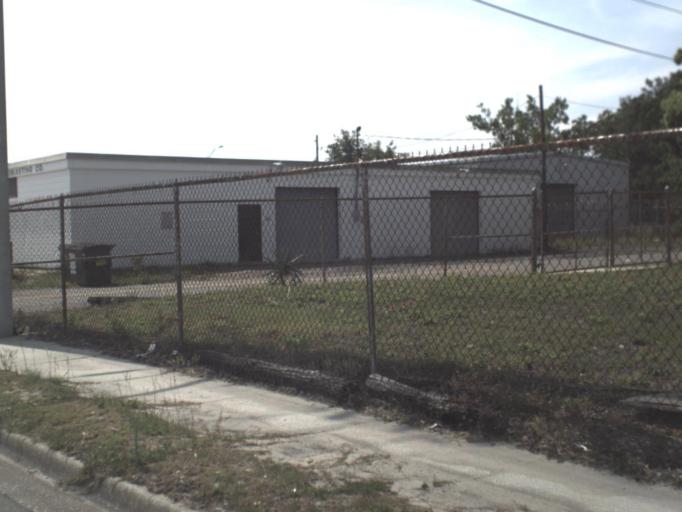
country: US
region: Florida
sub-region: Duval County
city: Jacksonville
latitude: 30.3454
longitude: -81.6350
